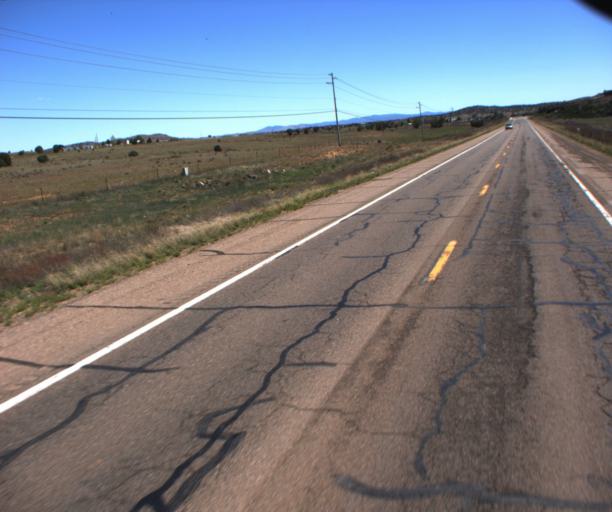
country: US
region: Arizona
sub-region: Yavapai County
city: Paulden
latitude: 34.8750
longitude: -112.4693
